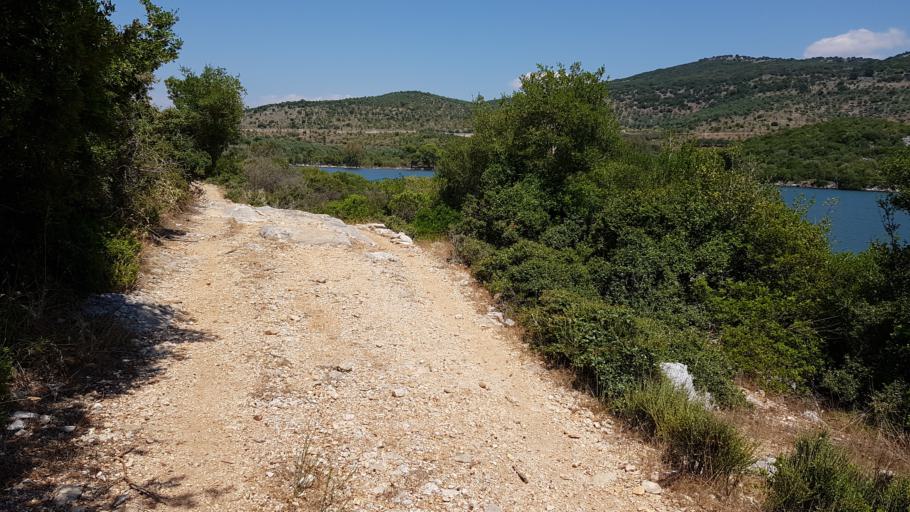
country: AL
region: Vlore
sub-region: Rrethi i Sarandes
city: Xarre
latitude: 39.7510
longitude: 19.9956
